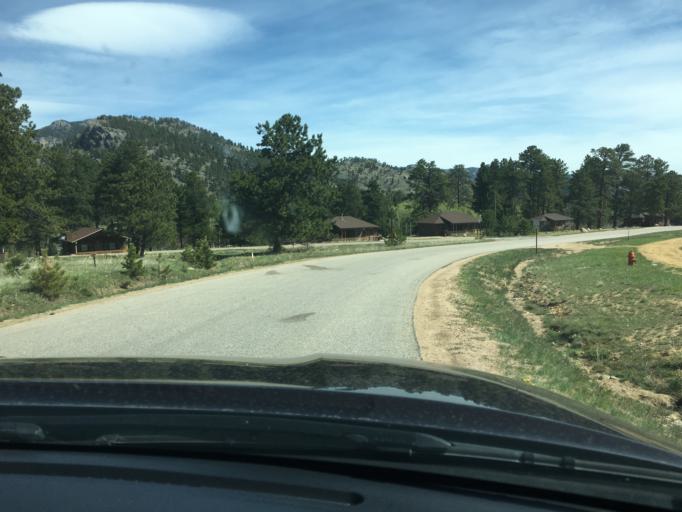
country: US
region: Colorado
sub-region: Larimer County
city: Estes Park
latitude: 40.3419
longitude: -105.5736
